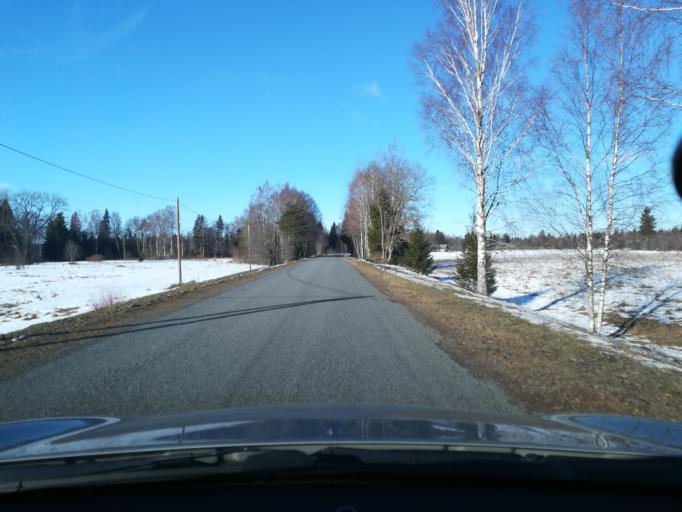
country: EE
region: Raplamaa
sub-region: Kohila vald
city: Kohila
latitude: 59.2371
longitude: 24.7559
